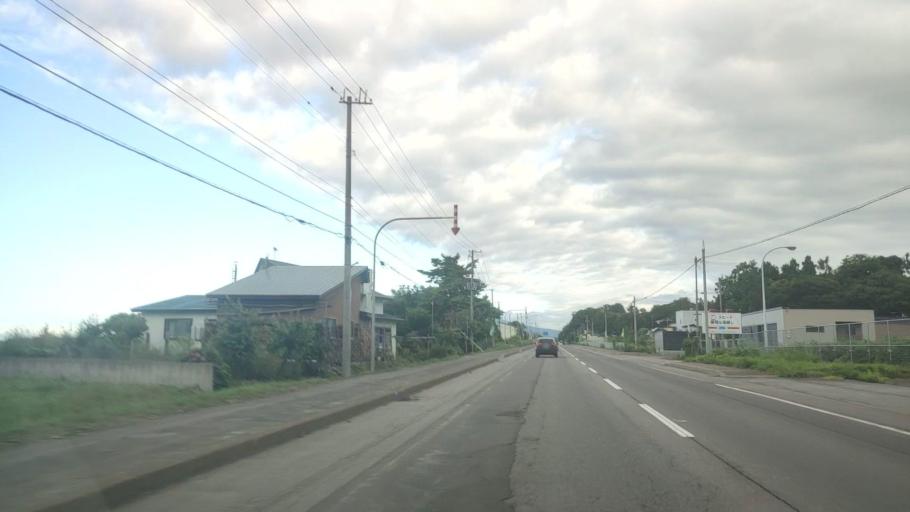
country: JP
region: Hokkaido
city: Nanae
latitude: 42.1164
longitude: 140.5400
